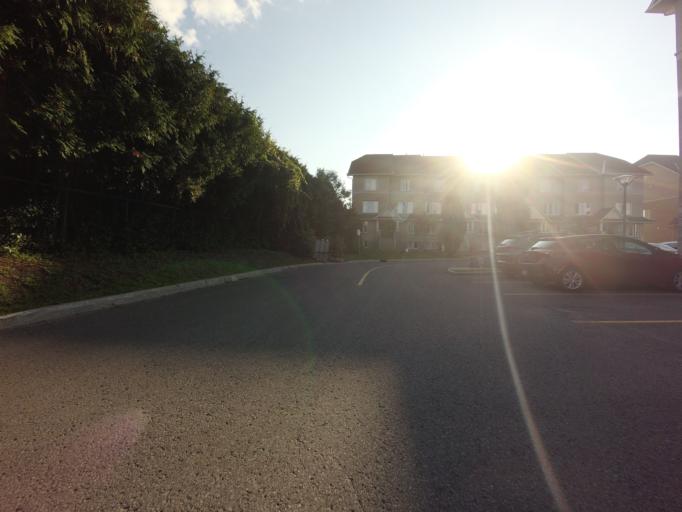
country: CA
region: Ontario
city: Bells Corners
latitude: 45.3419
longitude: -75.7641
